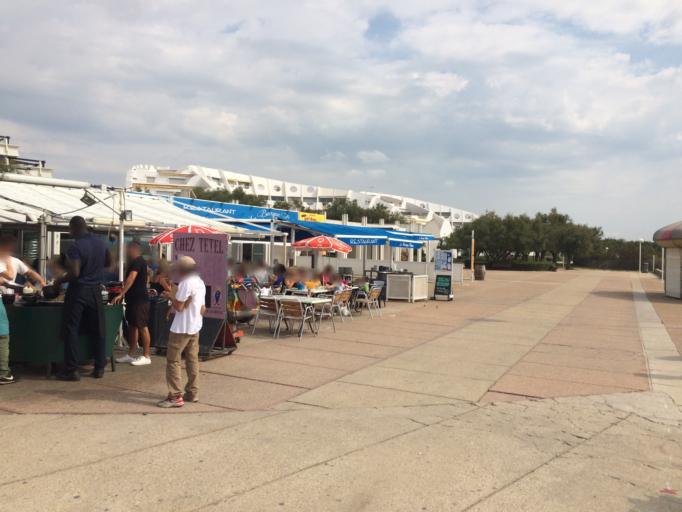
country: FR
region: Languedoc-Roussillon
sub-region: Departement de l'Herault
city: La Grande-Motte
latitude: 43.5580
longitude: 4.0705
